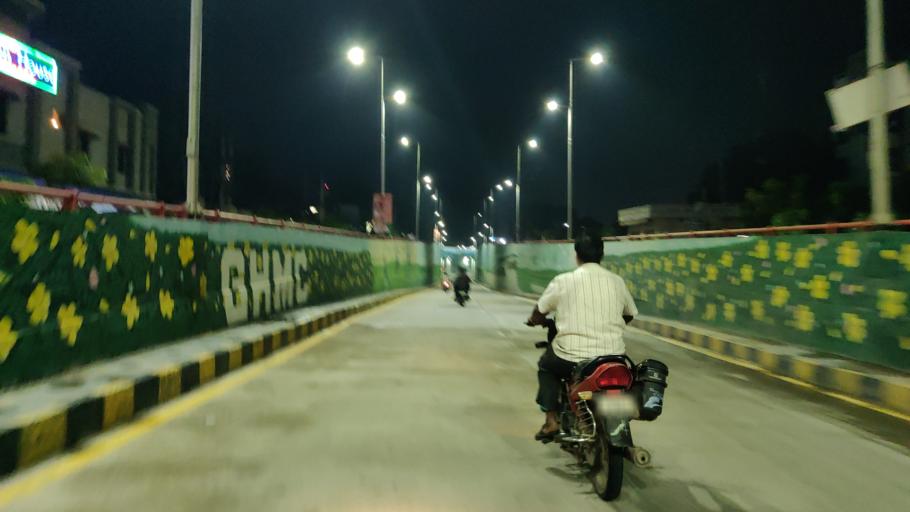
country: IN
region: Telangana
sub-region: Rangareddi
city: Lal Bahadur Nagar
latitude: 17.3420
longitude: 78.5548
